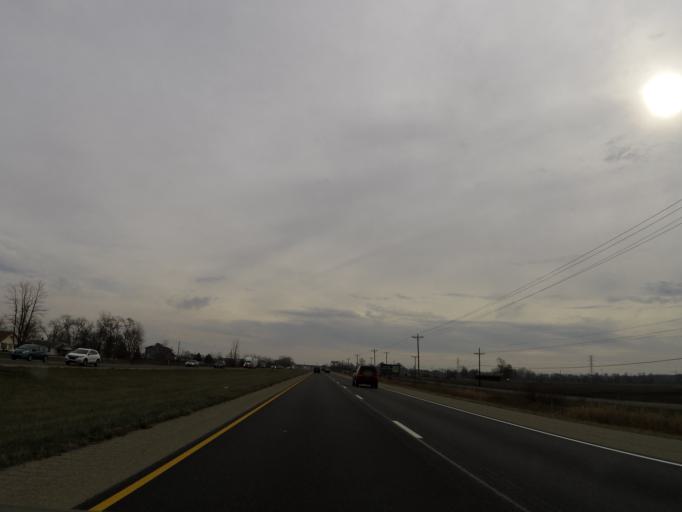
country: US
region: Indiana
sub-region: Shelby County
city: Shelbyville
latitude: 39.5691
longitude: -85.8019
